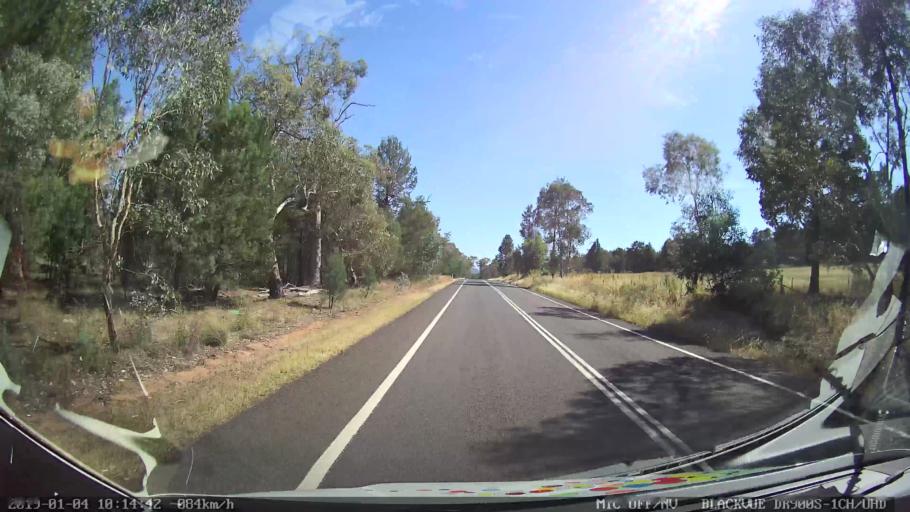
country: AU
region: New South Wales
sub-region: Cabonne
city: Canowindra
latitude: -33.3941
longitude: 148.4153
